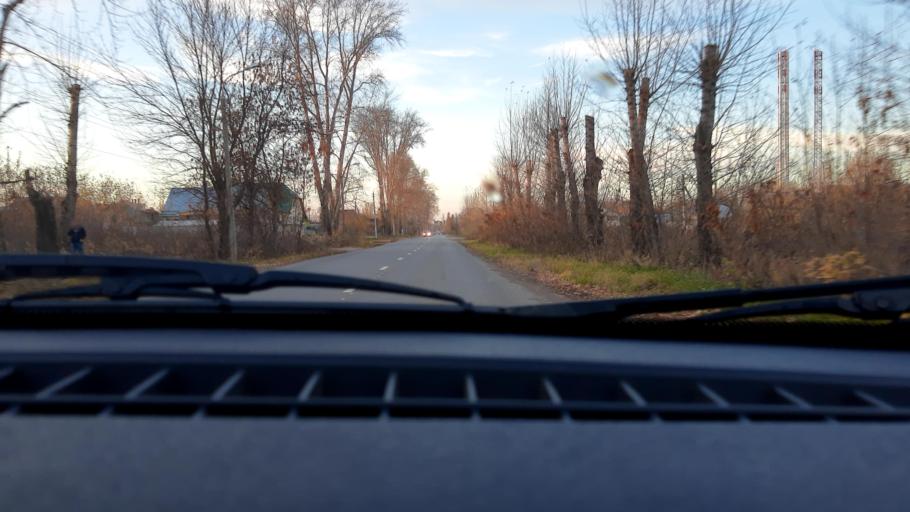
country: RU
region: Bashkortostan
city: Mikhaylovka
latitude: 54.7694
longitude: 55.8957
